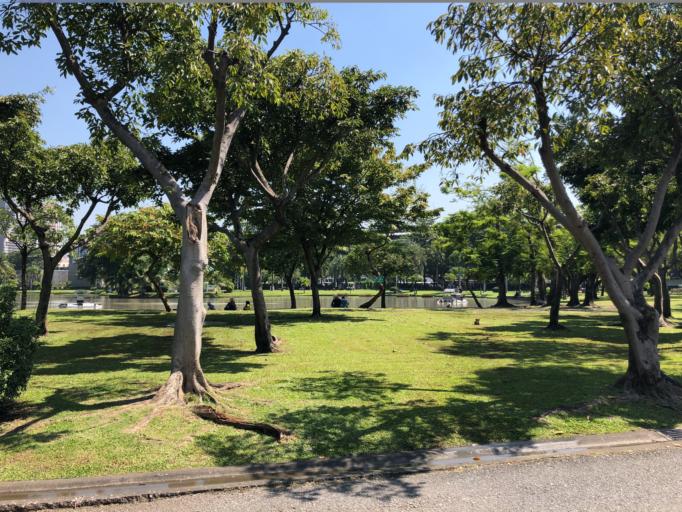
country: TH
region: Bangkok
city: Bang Sue
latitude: 13.8031
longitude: 100.5523
